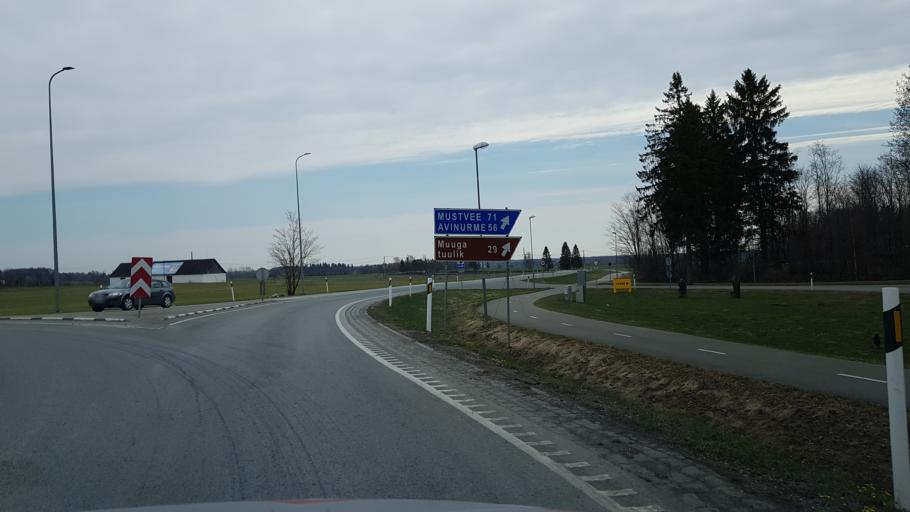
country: EE
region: Laeaene-Virumaa
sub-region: Rakvere linn
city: Rakvere
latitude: 59.3204
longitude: 26.3706
